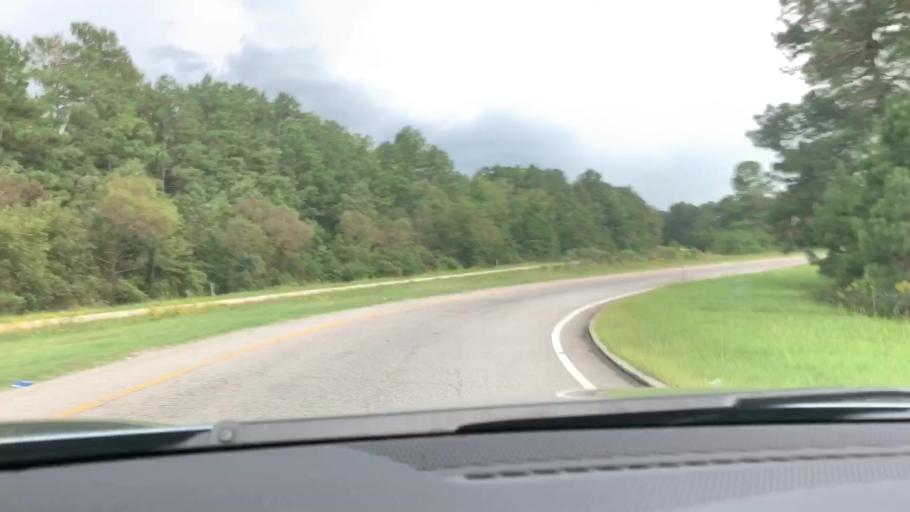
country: US
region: South Carolina
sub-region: Orangeburg County
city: Holly Hill
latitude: 33.3194
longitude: -80.5453
